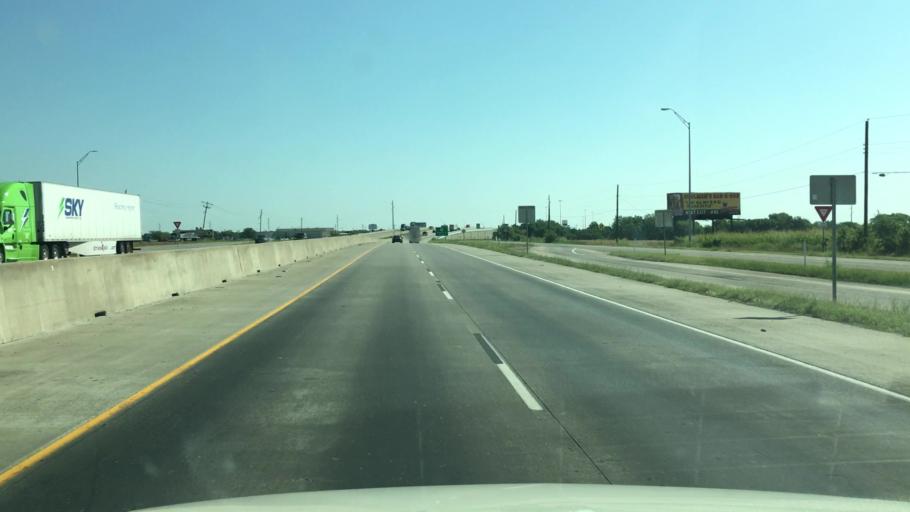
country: US
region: Texas
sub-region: Hunt County
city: Greenville
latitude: 33.0841
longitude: -96.1312
